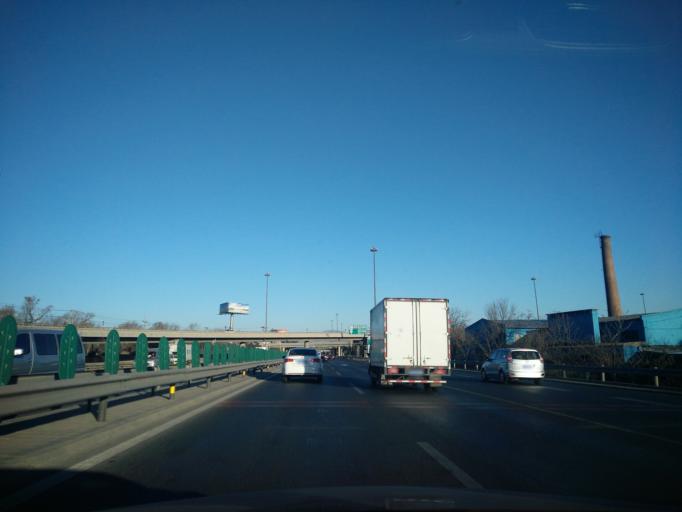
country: CN
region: Beijing
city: Fengtai
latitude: 39.8414
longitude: 116.2217
